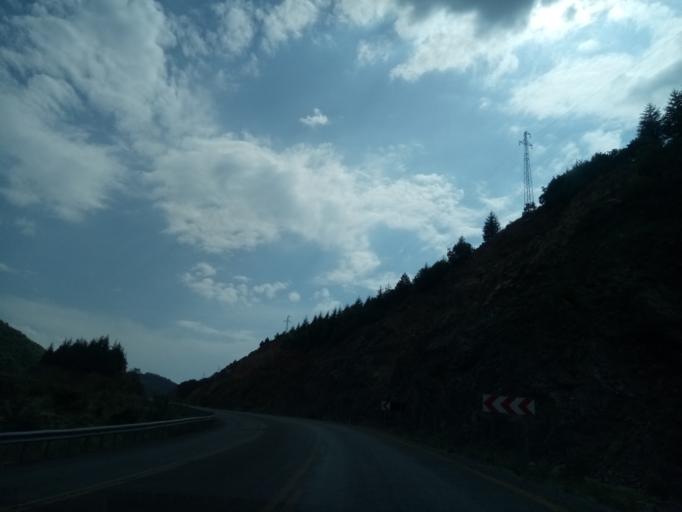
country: TR
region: Konya
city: Aksehir
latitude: 38.2902
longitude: 31.4407
